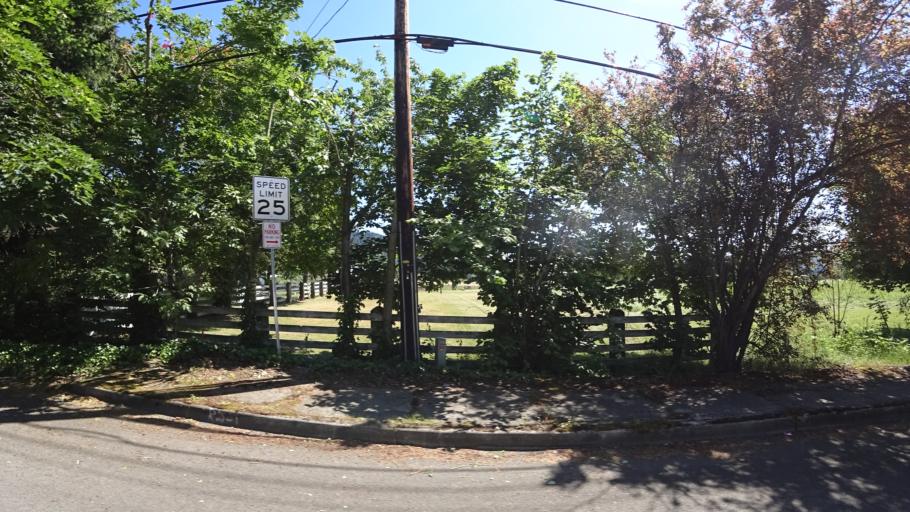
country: US
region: Oregon
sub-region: Multnomah County
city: Gresham
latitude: 45.4720
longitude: -122.4656
